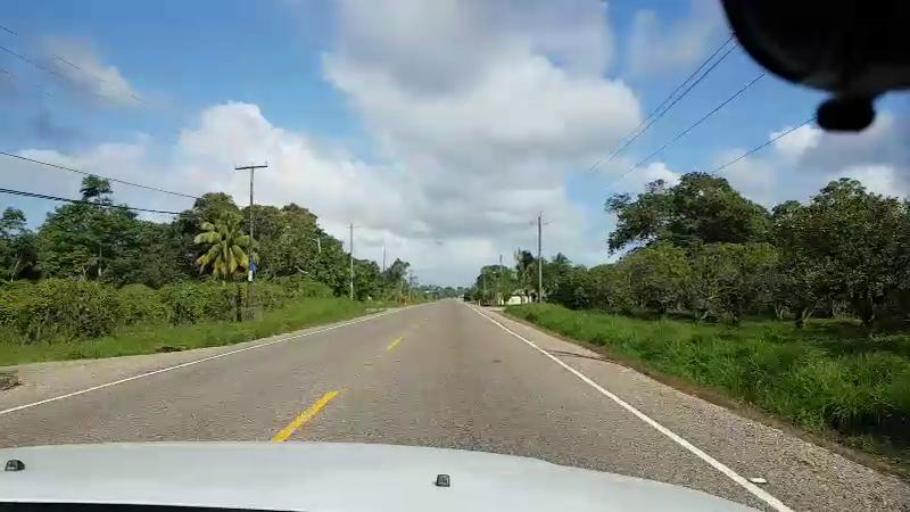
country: BZ
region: Stann Creek
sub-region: Dangriga
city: Dangriga
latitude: 16.9961
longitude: -88.3561
